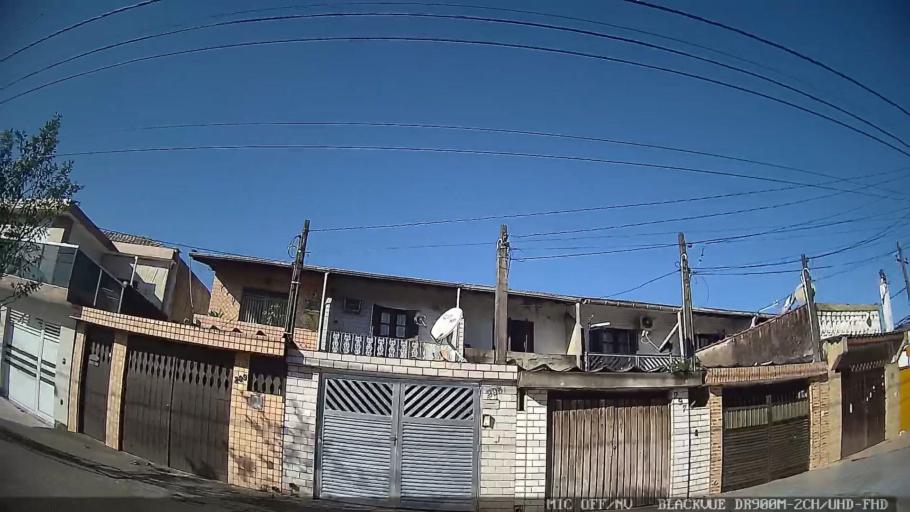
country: BR
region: Sao Paulo
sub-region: Guaruja
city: Guaruja
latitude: -23.9600
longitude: -46.2860
